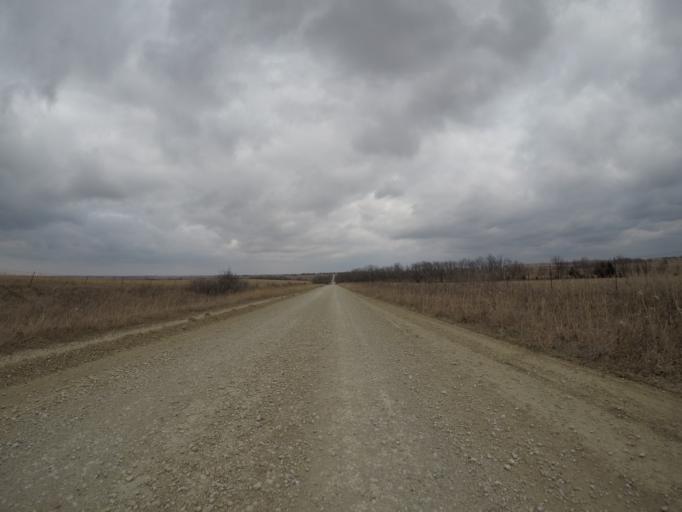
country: US
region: Kansas
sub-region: Morris County
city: Council Grove
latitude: 38.7286
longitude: -96.2794
